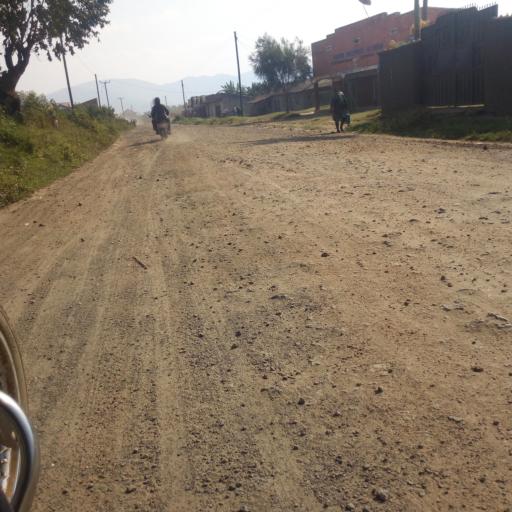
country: UG
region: Western Region
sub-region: Kisoro District
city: Kisoro
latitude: -1.2452
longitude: 29.7134
